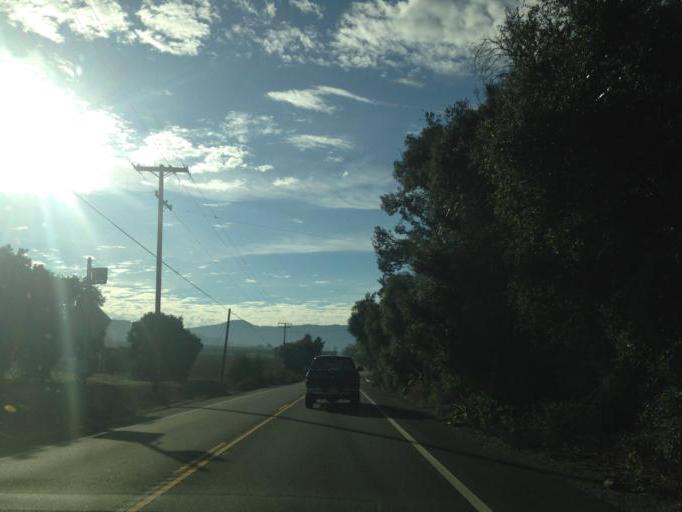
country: US
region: California
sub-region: San Diego County
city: Valley Center
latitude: 33.3277
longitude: -116.9994
